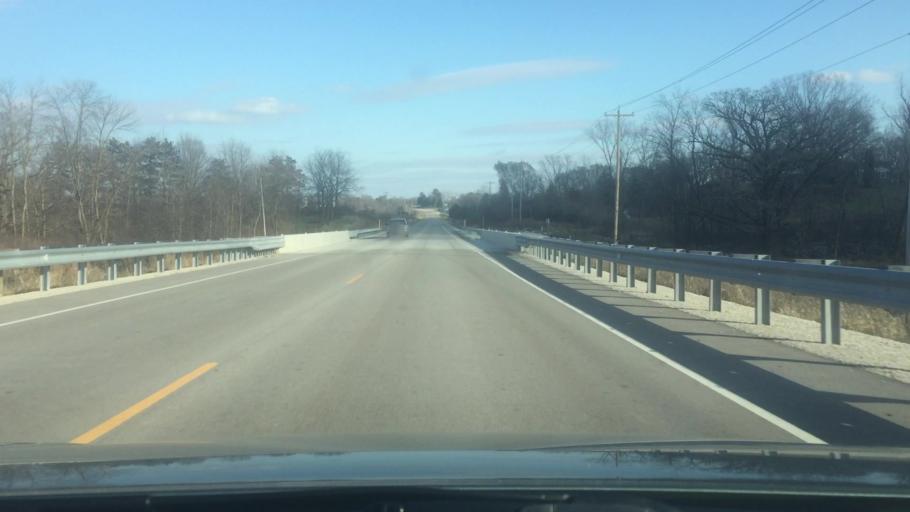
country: US
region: Wisconsin
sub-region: Walworth County
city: Whitewater
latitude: 42.9311
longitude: -88.6919
